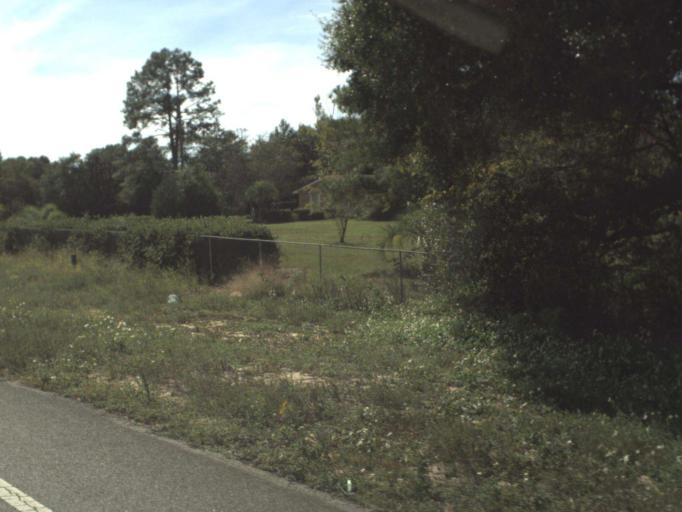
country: US
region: Florida
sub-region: Bay County
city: Lynn Haven
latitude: 30.4767
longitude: -85.6649
